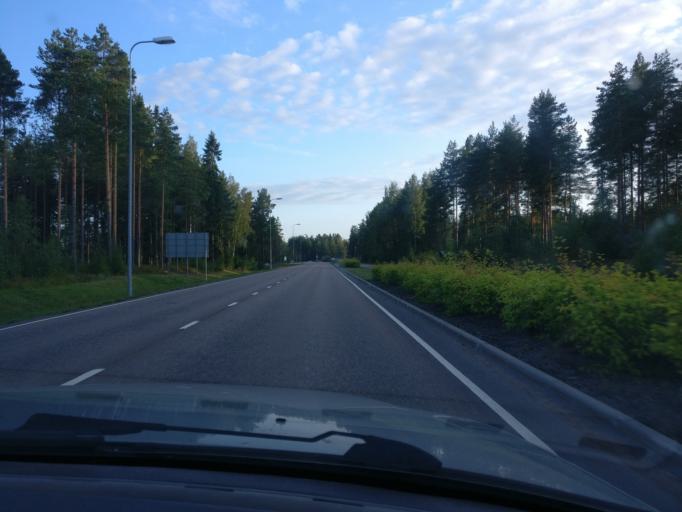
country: FI
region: Kymenlaakso
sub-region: Kotka-Hamina
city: Broby
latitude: 60.5004
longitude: 26.7406
